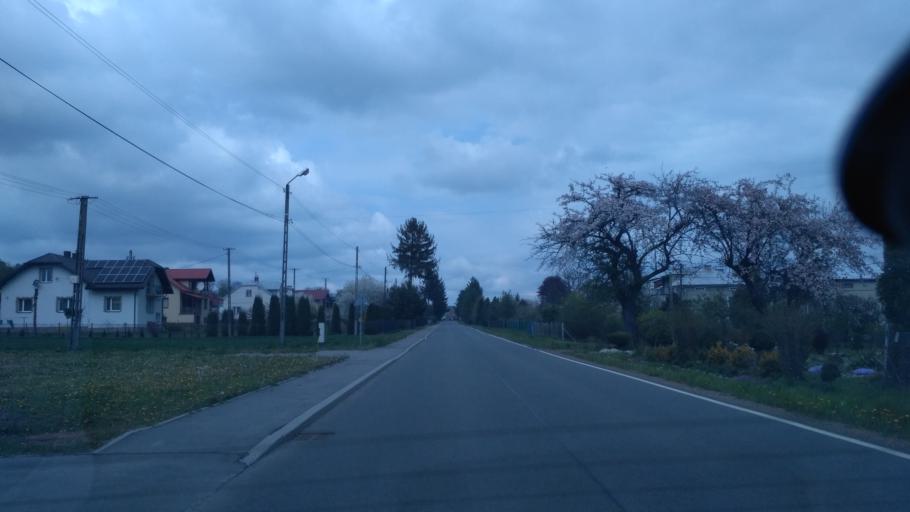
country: PL
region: Subcarpathian Voivodeship
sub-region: Powiat brzozowski
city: Jasionow
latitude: 49.6461
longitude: 21.9772
